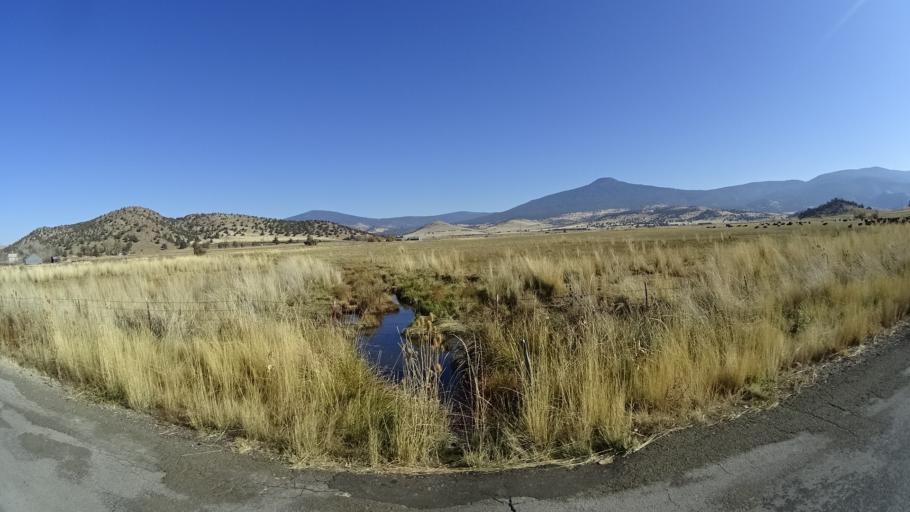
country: US
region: California
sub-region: Siskiyou County
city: Montague
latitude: 41.6954
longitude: -122.3750
